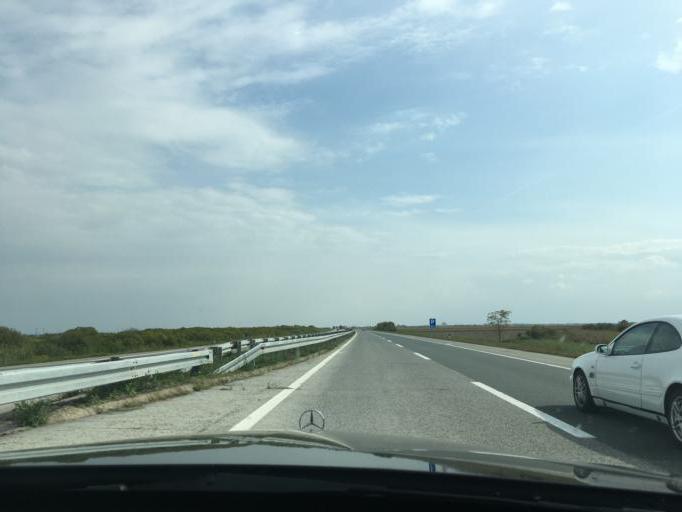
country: RS
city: Radenkovic
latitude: 45.0211
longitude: 19.5005
